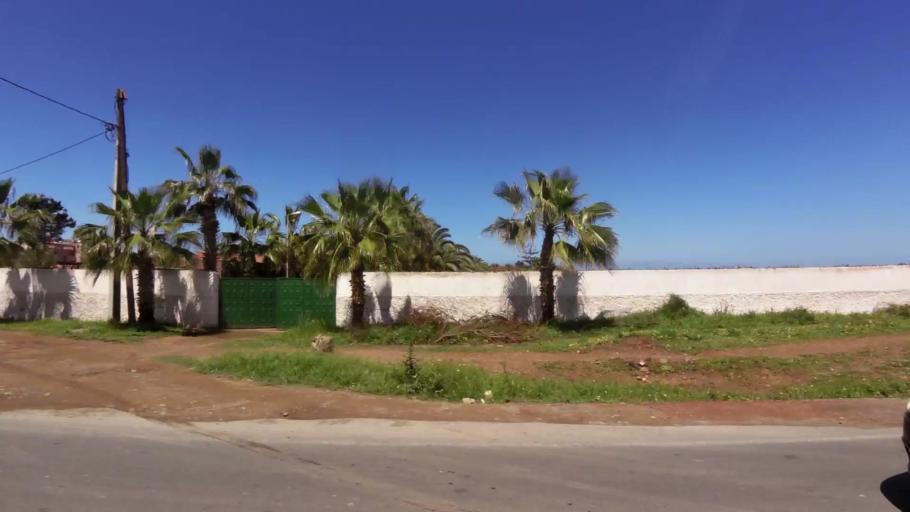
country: MA
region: Grand Casablanca
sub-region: Nouaceur
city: Dar Bouazza
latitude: 33.5184
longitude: -7.7974
